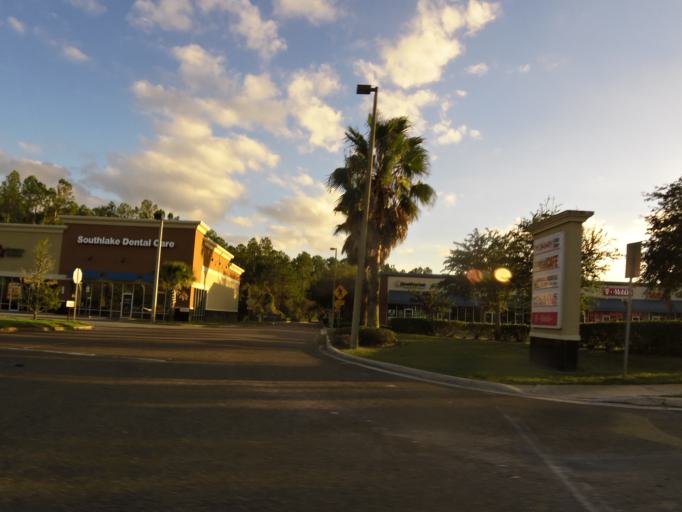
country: US
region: Florida
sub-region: Saint Johns County
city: Fruit Cove
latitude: 30.0599
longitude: -81.5136
